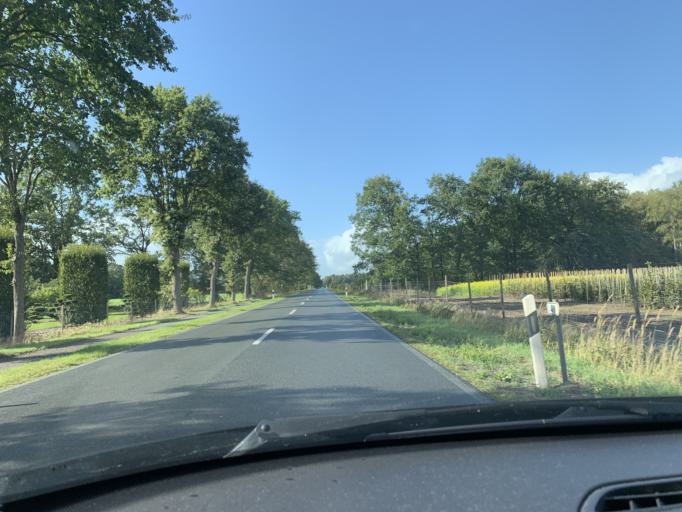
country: DE
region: Lower Saxony
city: Westerstede
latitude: 53.1879
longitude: 7.9239
